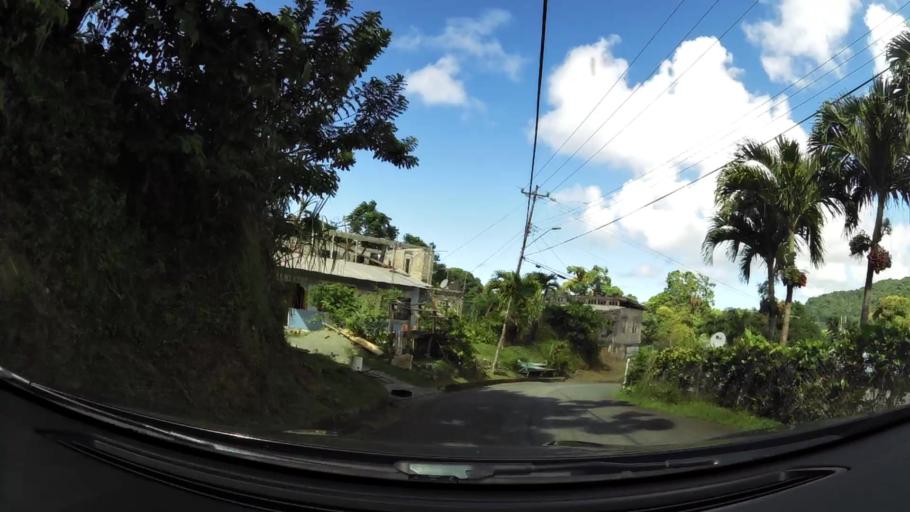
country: TT
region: Eastern Tobago
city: Roxborough
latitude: 11.3105
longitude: -60.6183
